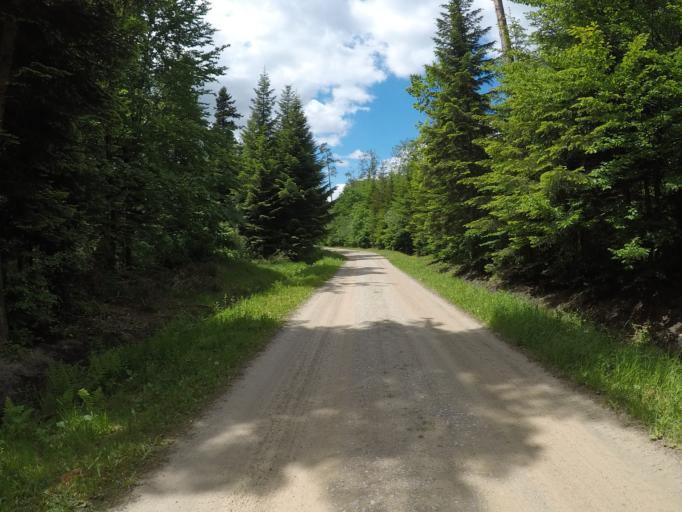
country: PL
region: Swietokrzyskie
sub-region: Powiat kielecki
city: Kostomloty Pierwsze
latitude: 50.9327
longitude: 20.6449
